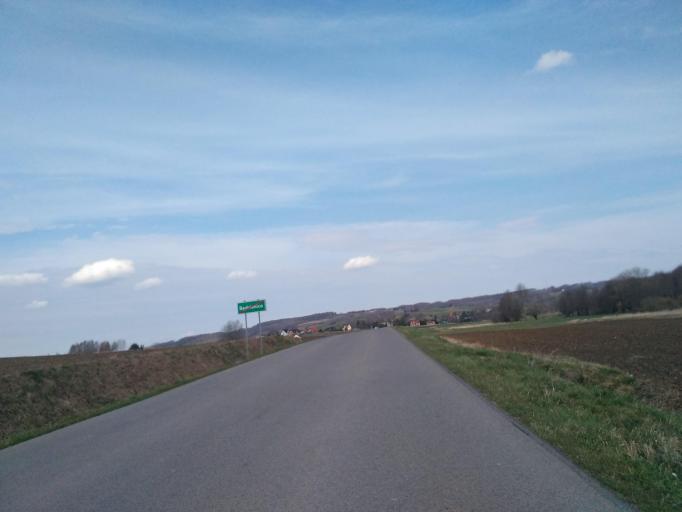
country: PL
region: Subcarpathian Voivodeship
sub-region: Powiat ropczycko-sedziszowski
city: Iwierzyce
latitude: 50.0091
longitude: 21.7898
